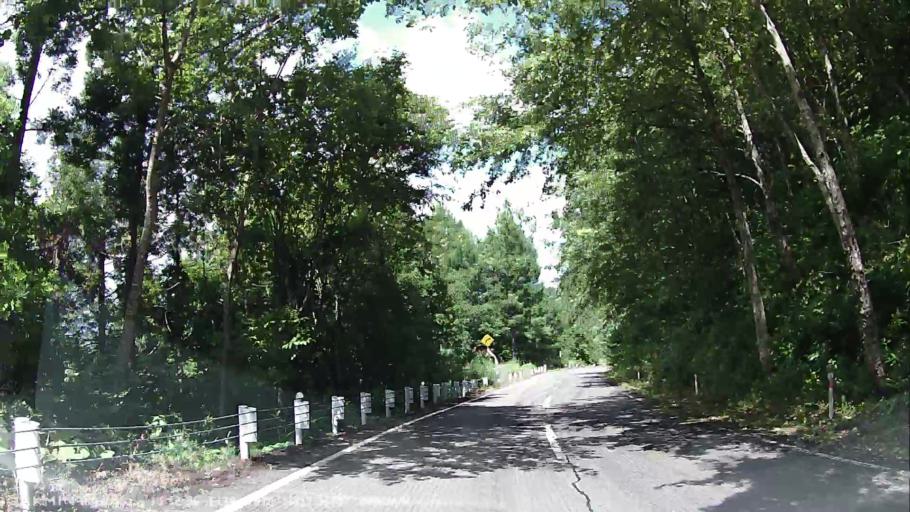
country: JP
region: Fukushima
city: Kitakata
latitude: 37.3675
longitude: 139.8787
